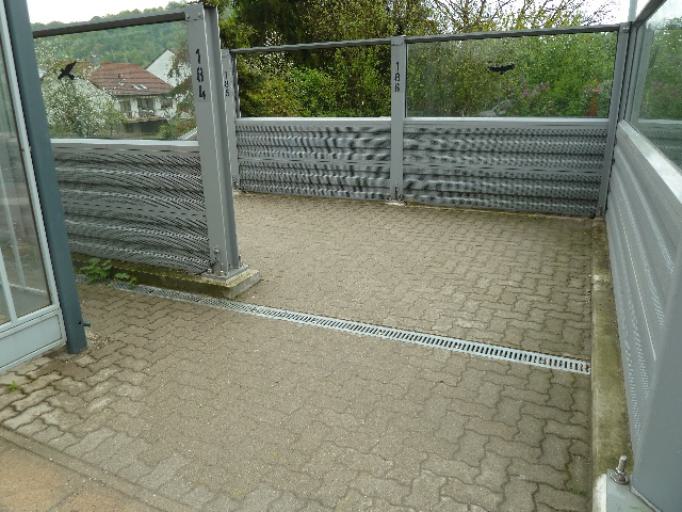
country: DE
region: Baden-Wuerttemberg
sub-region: Karlsruhe Region
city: Weingarten
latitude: 49.0878
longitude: 8.5485
